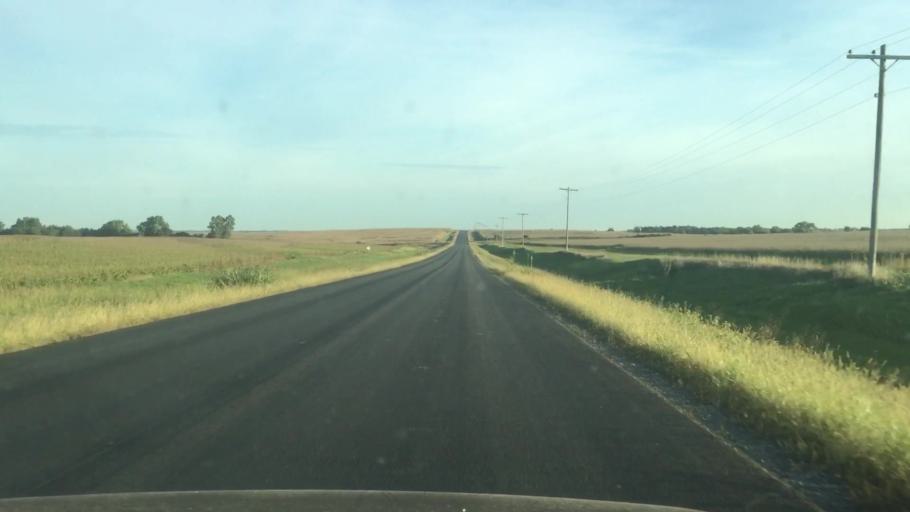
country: US
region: Kansas
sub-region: Marshall County
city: Marysville
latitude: 39.9096
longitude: -96.6010
